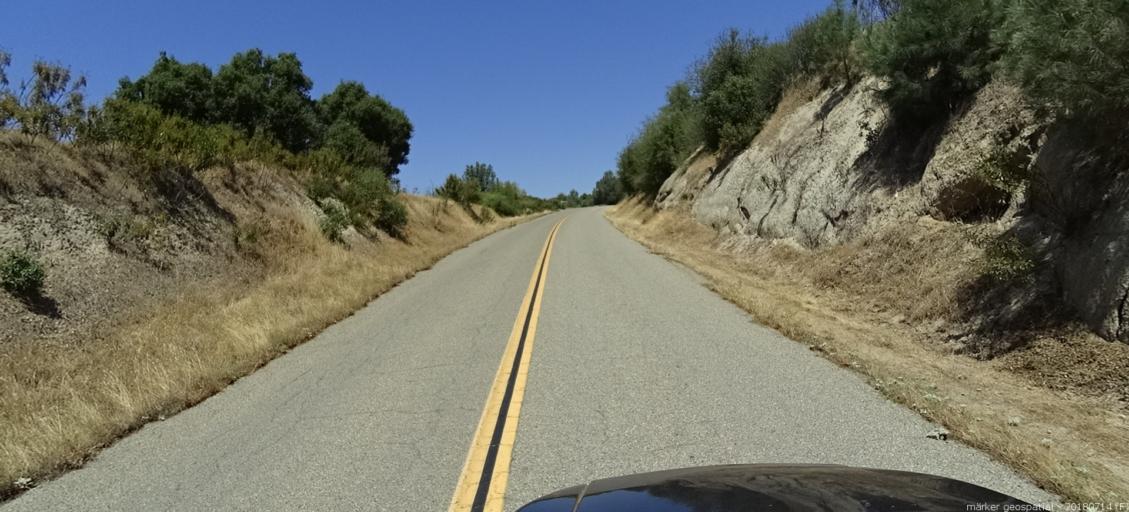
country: US
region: California
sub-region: Madera County
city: Ahwahnee
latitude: 37.3852
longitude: -119.7170
